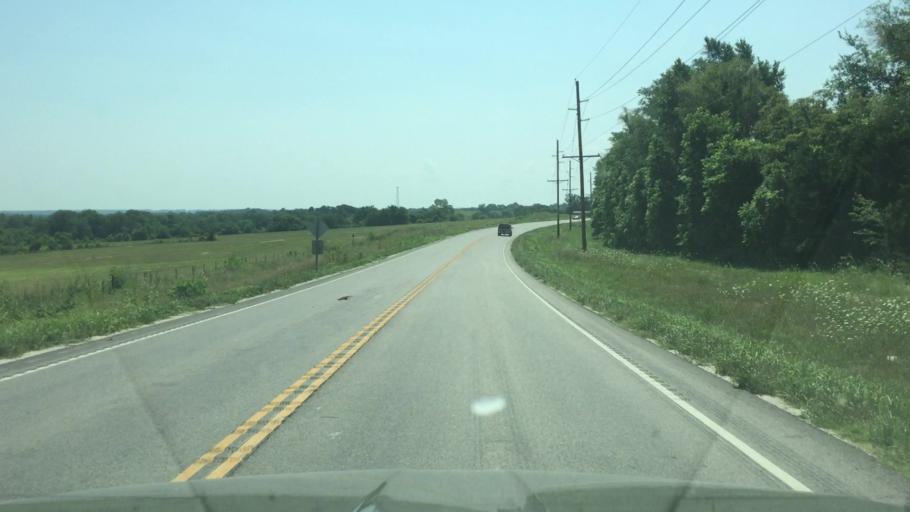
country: US
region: Missouri
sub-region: Miller County
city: Eldon
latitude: 38.3868
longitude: -92.6927
